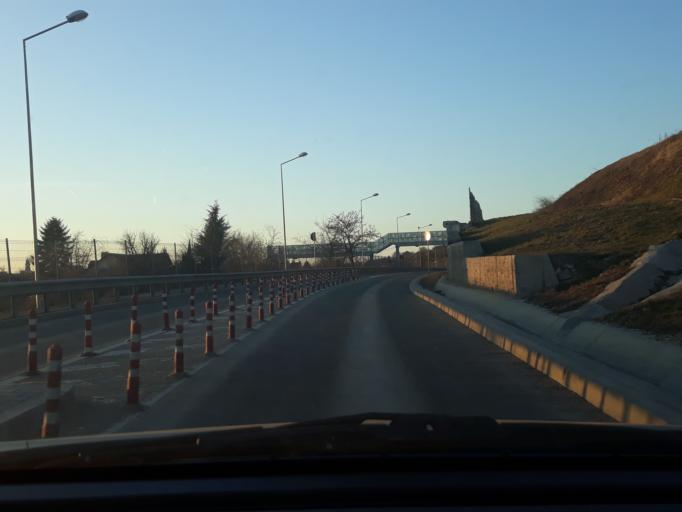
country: RO
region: Bihor
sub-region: Comuna Biharea
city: Oradea
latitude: 47.0562
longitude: 21.9494
